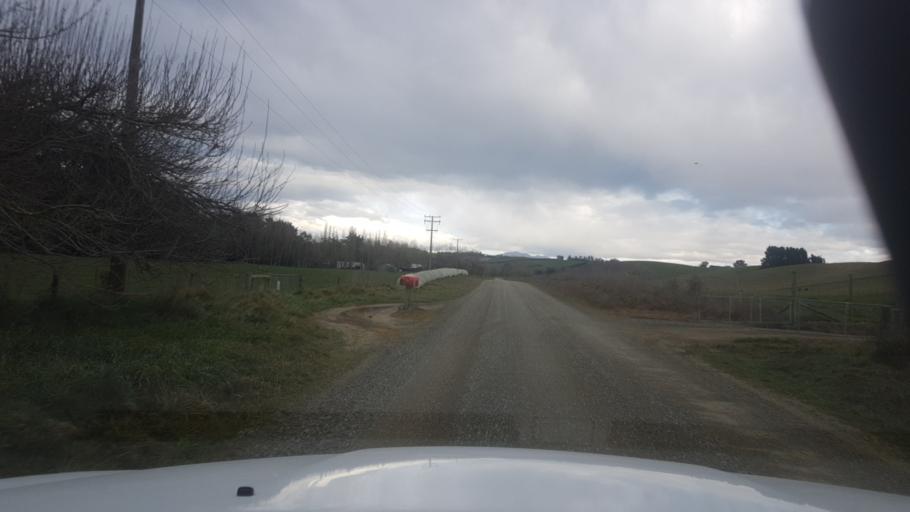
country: NZ
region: Canterbury
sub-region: Timaru District
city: Pleasant Point
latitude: -44.3389
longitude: 171.1755
